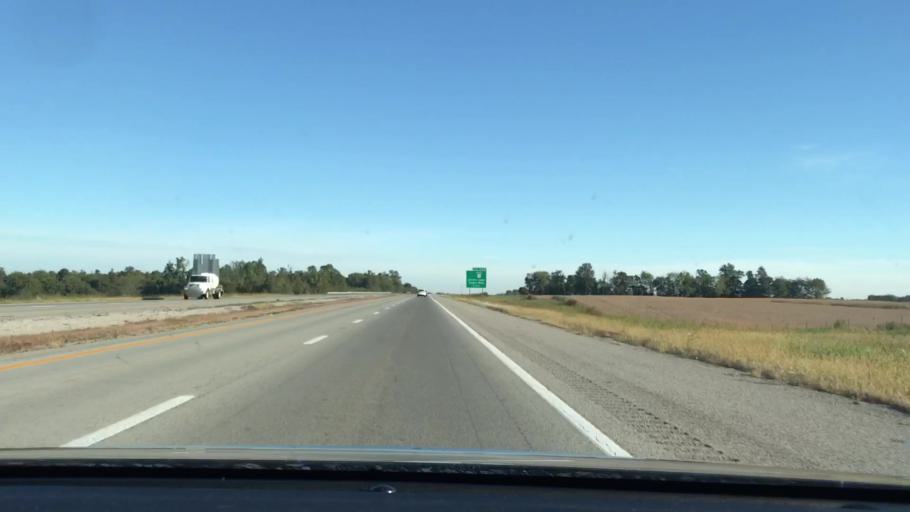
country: US
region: Kentucky
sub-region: Christian County
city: Hopkinsville
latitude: 36.7747
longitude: -87.4984
